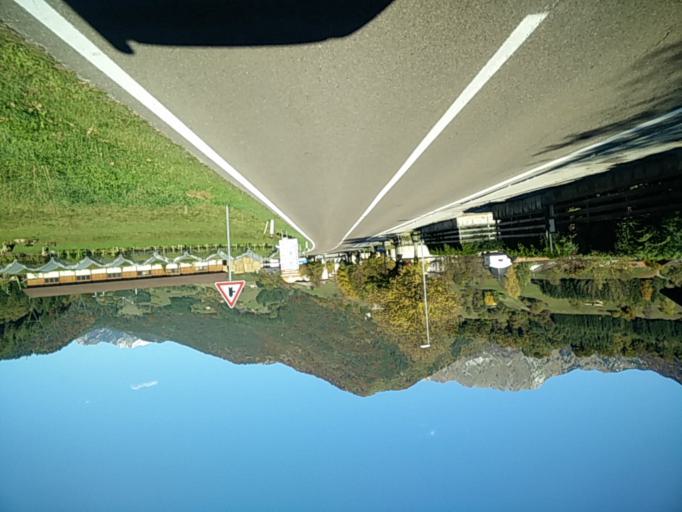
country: IT
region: Trentino-Alto Adige
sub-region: Provincia di Trento
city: Prezzo
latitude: 45.8865
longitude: 10.6693
